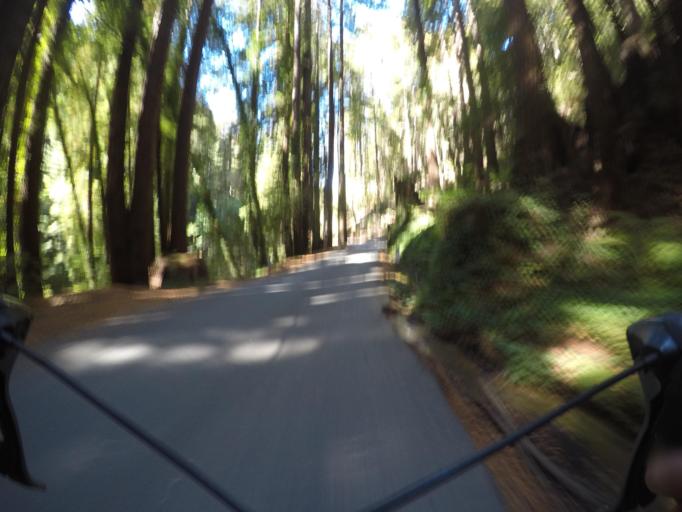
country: US
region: California
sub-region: San Mateo County
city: Portola Valley
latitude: 37.2988
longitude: -122.2630
